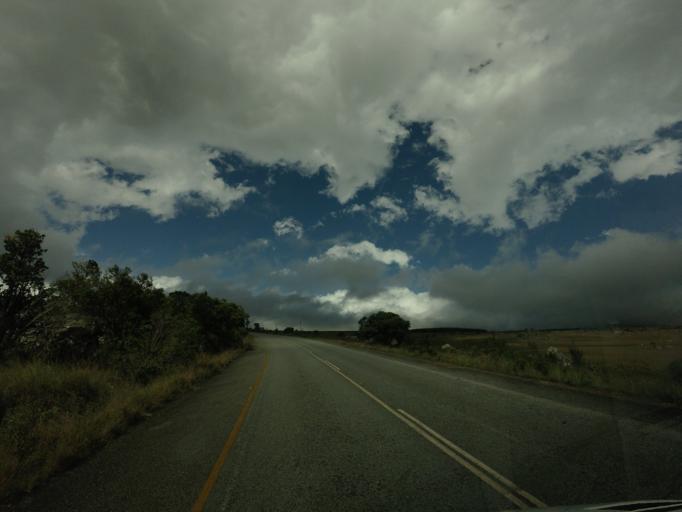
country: ZA
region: Mpumalanga
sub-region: Ehlanzeni District
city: Graksop
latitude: -24.8621
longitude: 30.8629
